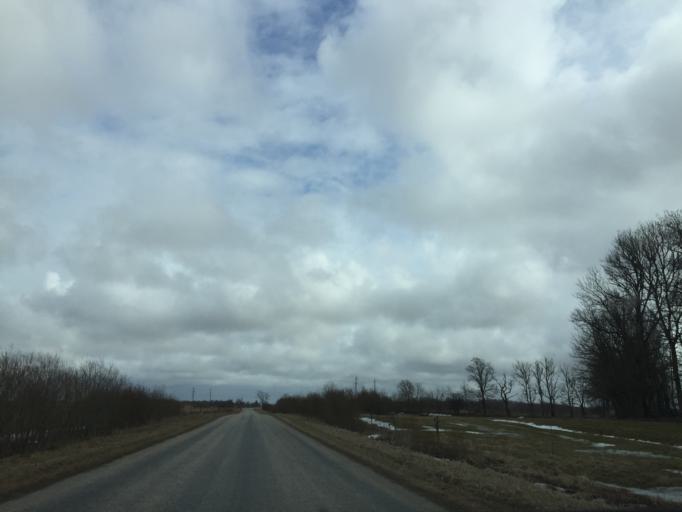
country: EE
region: Laeaene
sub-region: Lihula vald
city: Lihula
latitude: 58.7274
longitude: 23.9028
